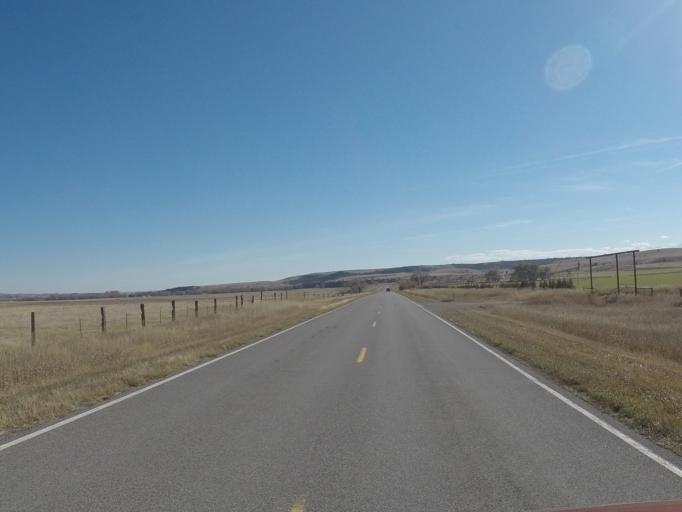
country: US
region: Montana
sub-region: Sweet Grass County
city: Big Timber
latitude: 45.8025
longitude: -109.8642
